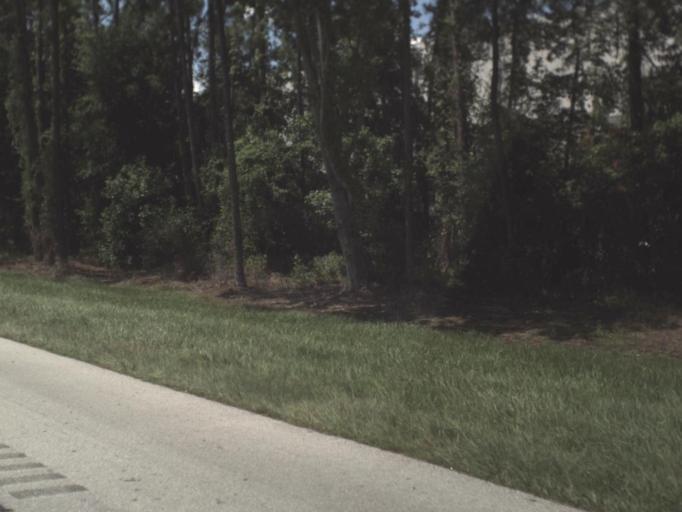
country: US
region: Florida
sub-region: Saint Johns County
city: Saint Augustine South
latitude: 29.8356
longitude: -81.3843
